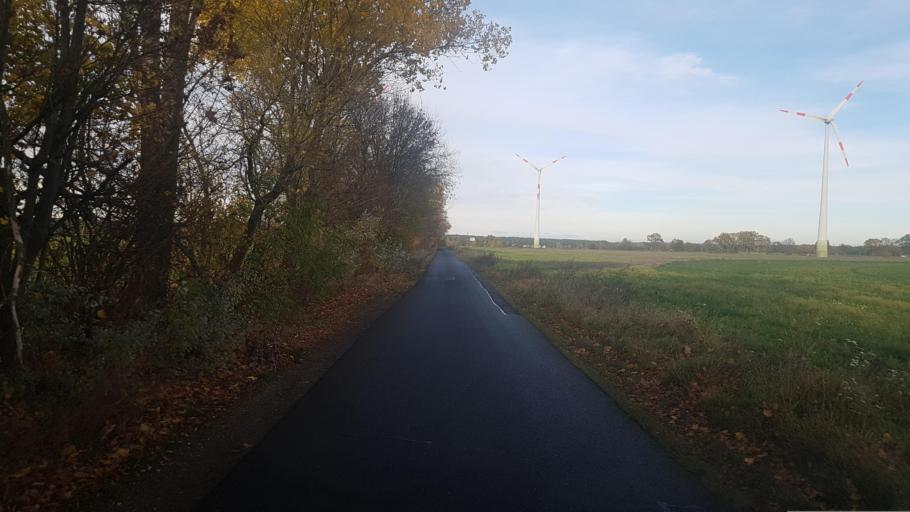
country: DE
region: Saxony-Anhalt
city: Muhlanger
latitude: 51.8628
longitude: 12.7328
